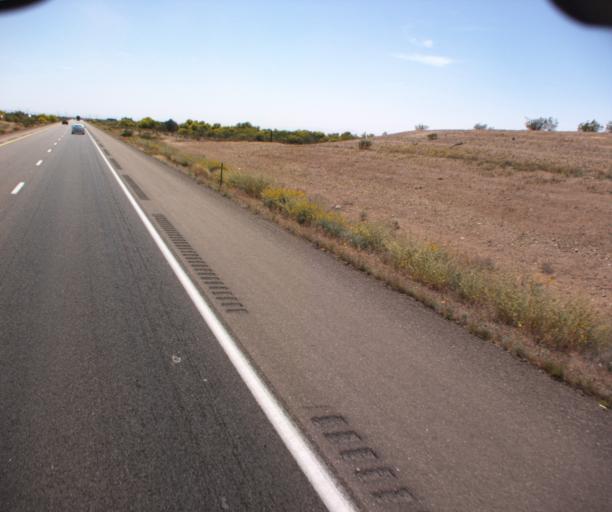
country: US
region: Arizona
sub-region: Maricopa County
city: Gila Bend
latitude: 33.0633
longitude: -112.6453
